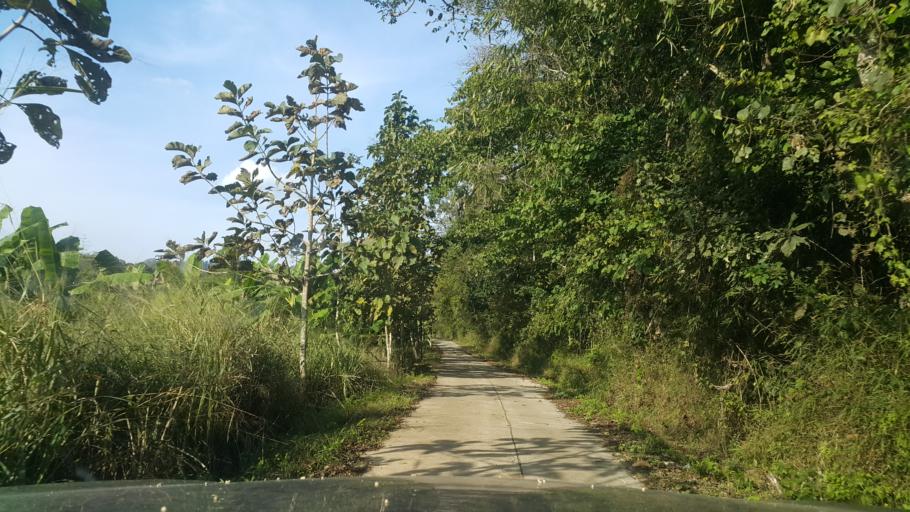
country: TH
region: Chiang Mai
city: Samoeng
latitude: 18.9942
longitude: 98.6849
